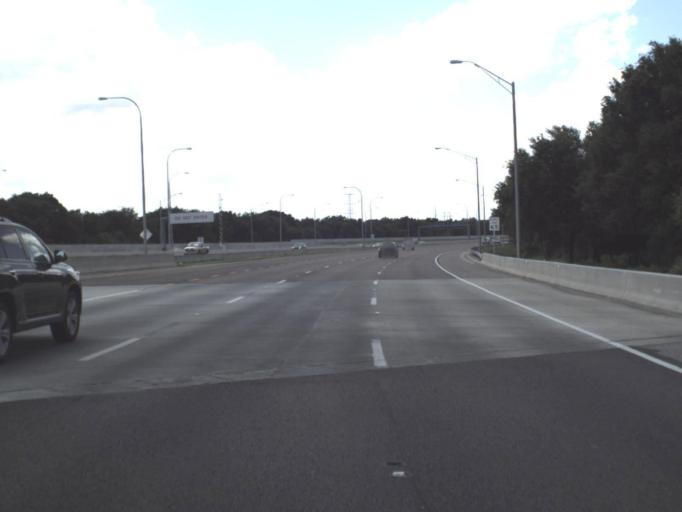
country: US
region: Florida
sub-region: Hillsborough County
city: Palm River-Clair Mel
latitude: 27.9326
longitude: -82.3555
